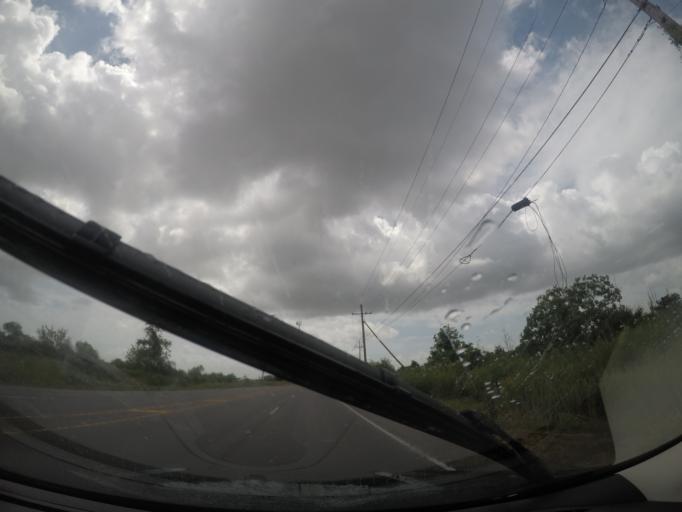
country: US
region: Louisiana
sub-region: Saint Tammany Parish
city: Eden Isle
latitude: 30.0762
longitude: -89.8439
